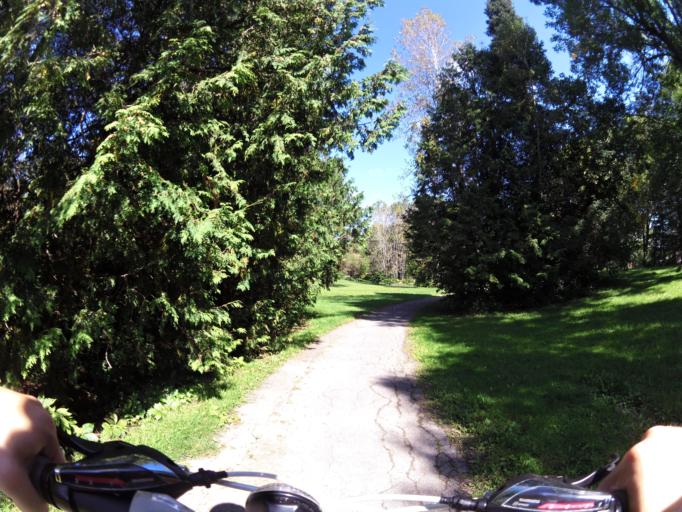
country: CA
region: Ontario
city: Bells Corners
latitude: 45.3238
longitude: -75.9067
